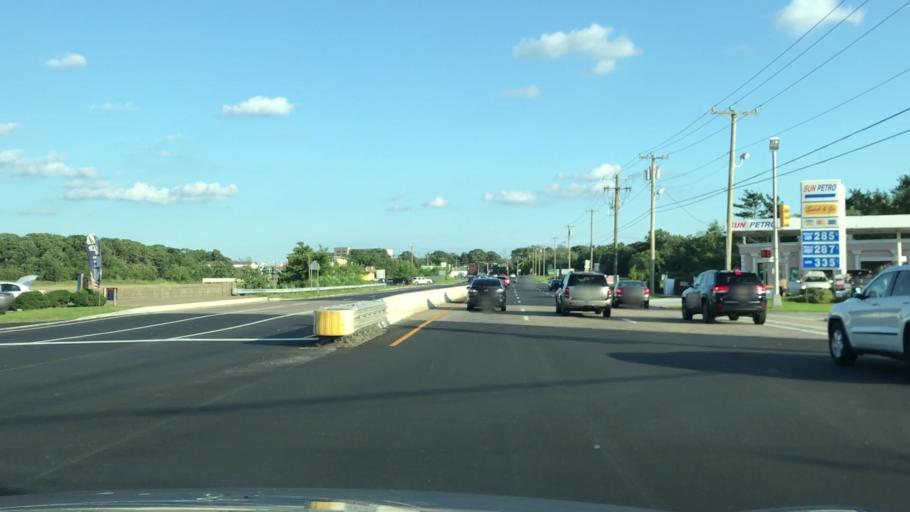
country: US
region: New Jersey
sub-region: Atlantic County
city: Absecon
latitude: 39.4231
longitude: -74.4997
